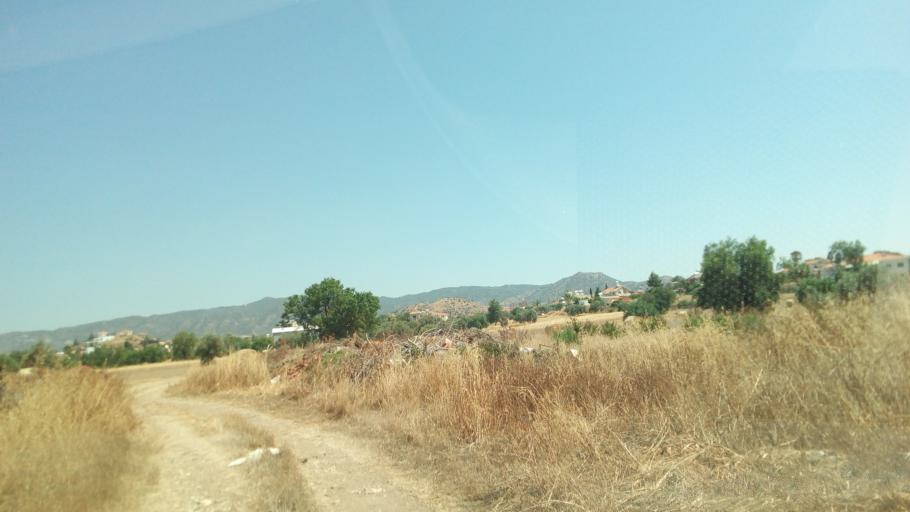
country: CY
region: Limassol
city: Pyrgos
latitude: 34.7362
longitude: 33.1814
